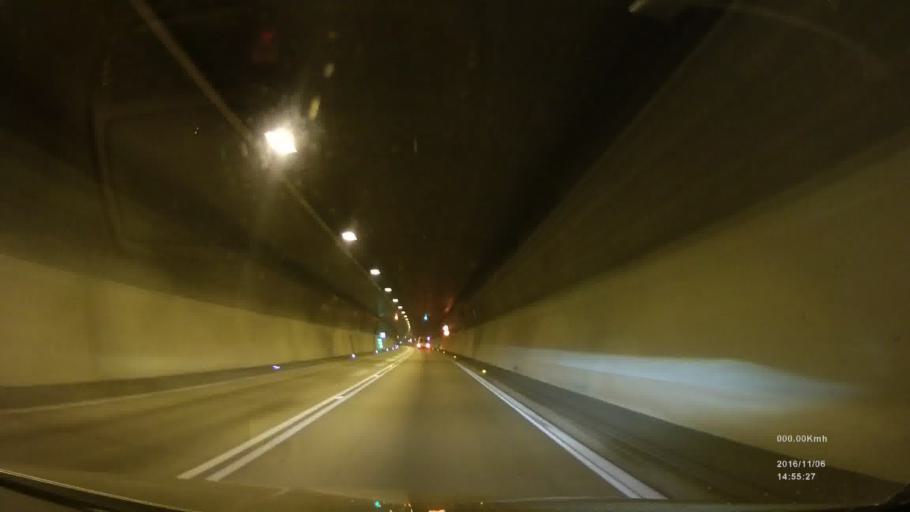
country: SK
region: Kosicky
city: Krompachy
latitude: 48.9996
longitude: 20.8920
